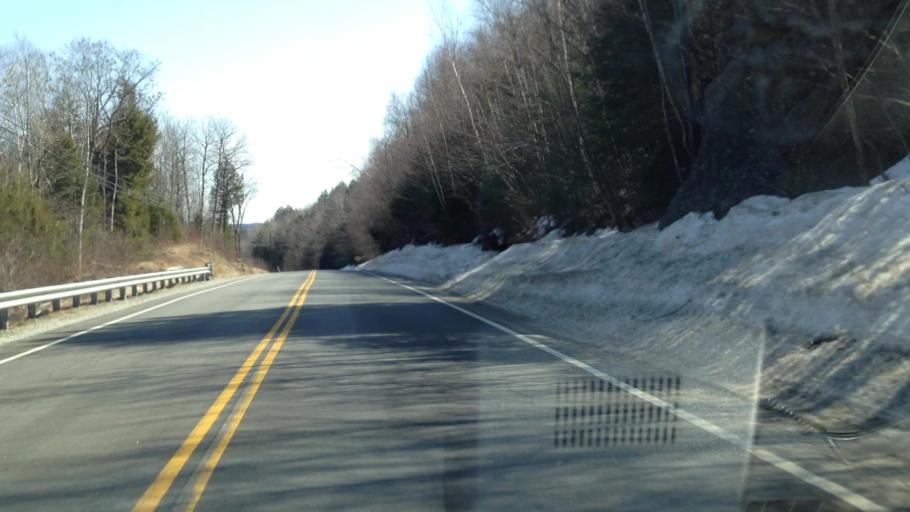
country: US
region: New Hampshire
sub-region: Merrimack County
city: Wilmot
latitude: 43.4631
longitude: -71.9556
